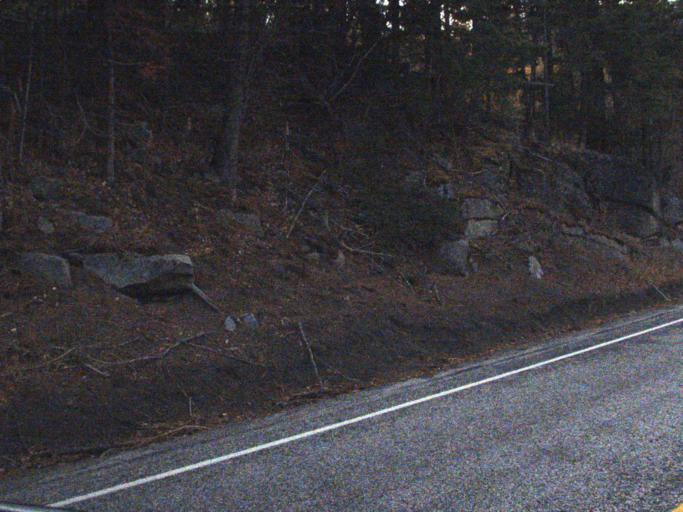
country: US
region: Washington
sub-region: Ferry County
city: Republic
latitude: 48.6005
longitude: -118.5336
